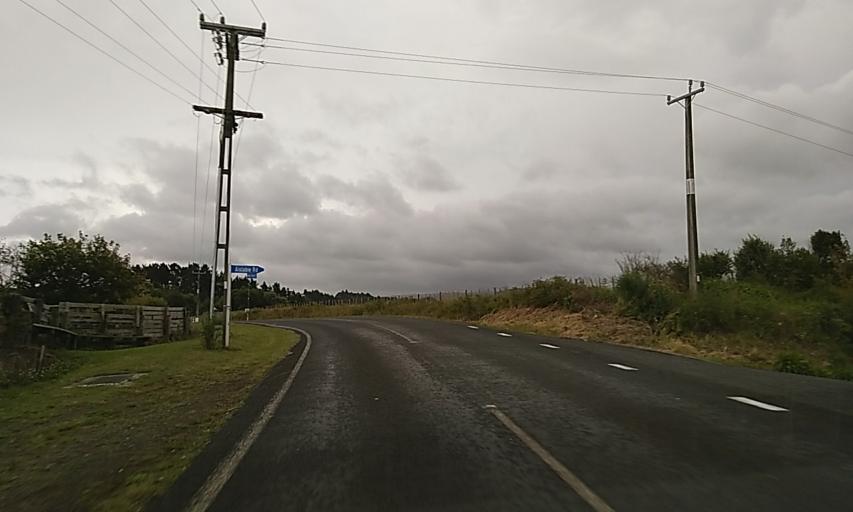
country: NZ
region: Auckland
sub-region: Auckland
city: Pukekohe East
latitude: -37.3211
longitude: 174.9211
